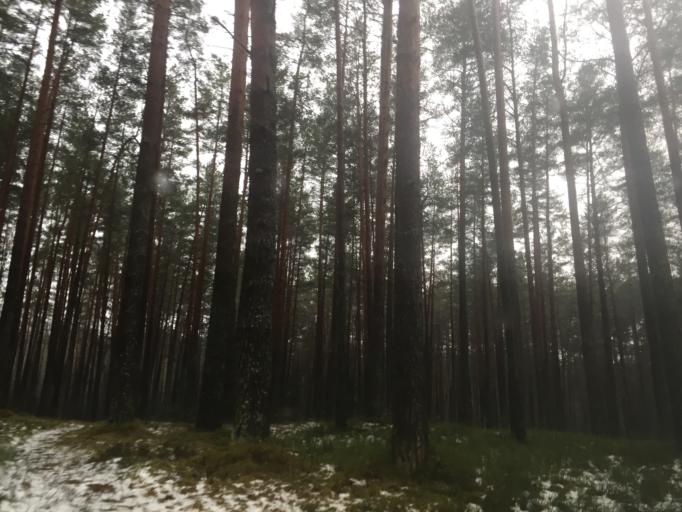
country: LV
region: Stopini
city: Ulbroka
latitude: 56.9529
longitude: 24.3374
